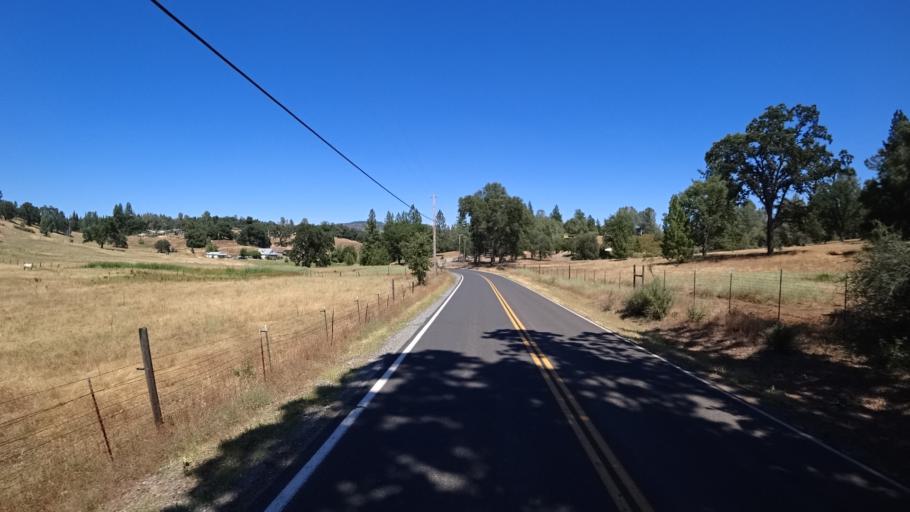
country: US
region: California
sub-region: Calaveras County
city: Mountain Ranch
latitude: 38.2860
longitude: -120.5007
